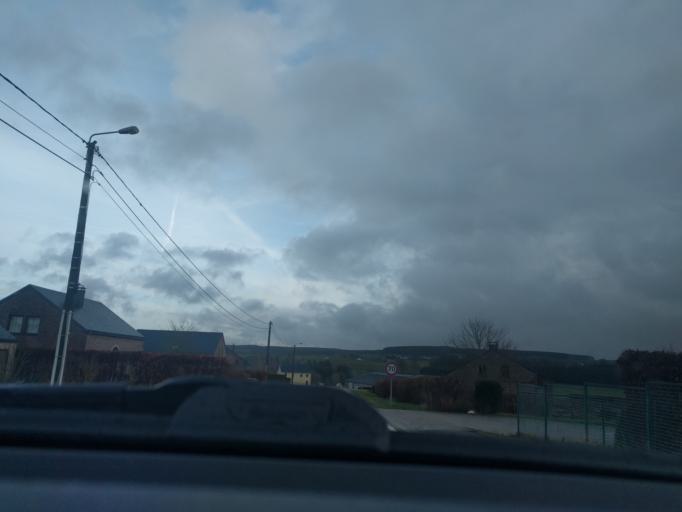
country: BE
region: Wallonia
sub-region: Province du Luxembourg
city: Gouvy
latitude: 50.1880
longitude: 5.9646
